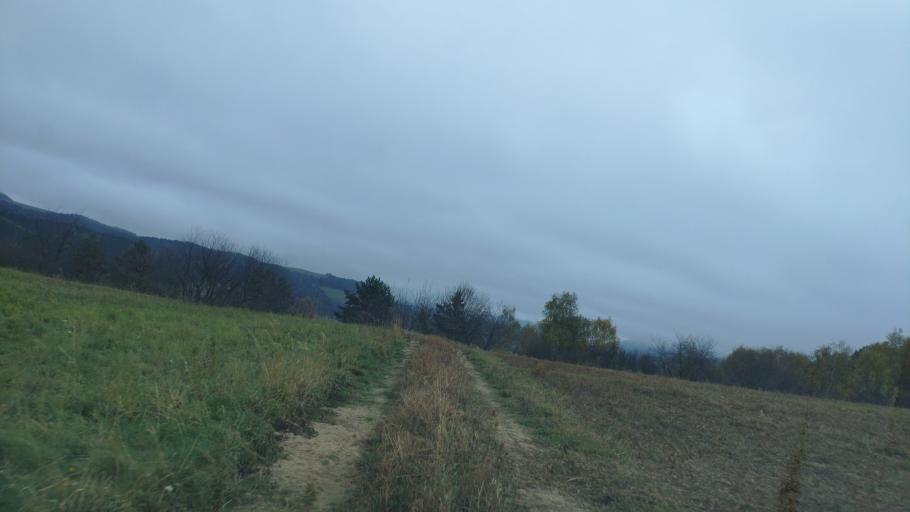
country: SK
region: Presovsky
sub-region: Okres Presov
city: Presov
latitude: 48.9305
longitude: 21.0951
